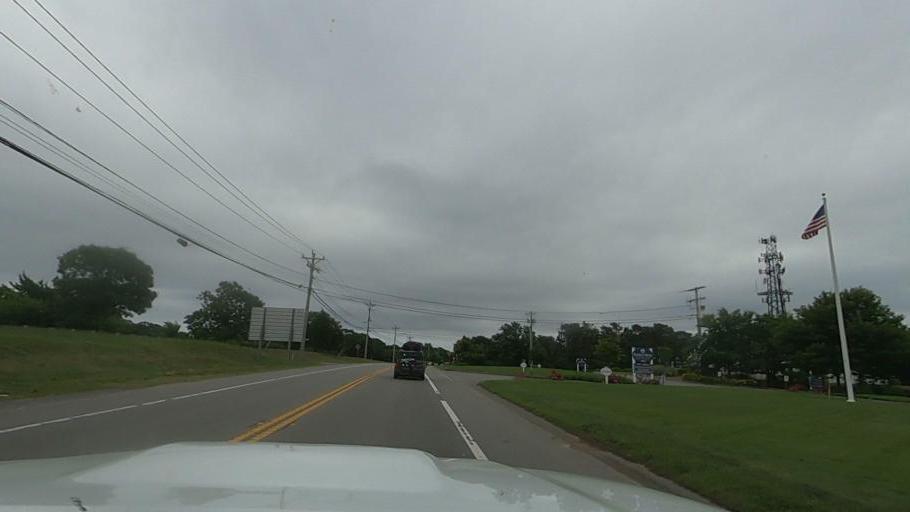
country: US
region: Massachusetts
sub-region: Barnstable County
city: Truro
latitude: 42.0238
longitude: -70.0746
